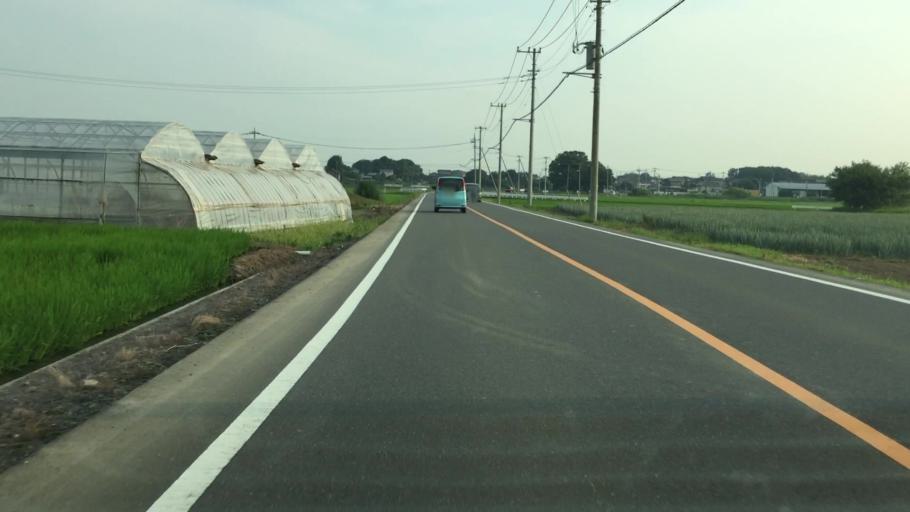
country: JP
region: Tochigi
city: Fujioka
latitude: 36.2404
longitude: 139.5938
